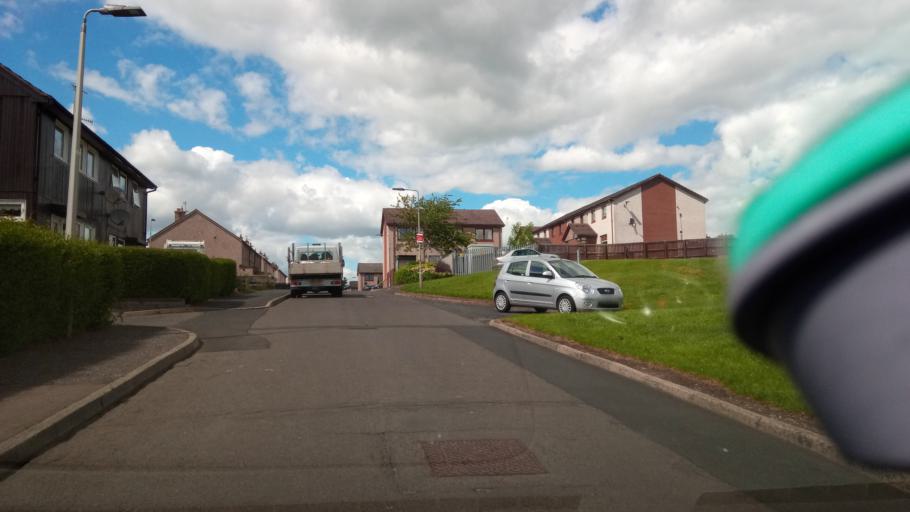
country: GB
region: Scotland
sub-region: The Scottish Borders
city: Jedburgh
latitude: 55.4700
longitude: -2.5467
